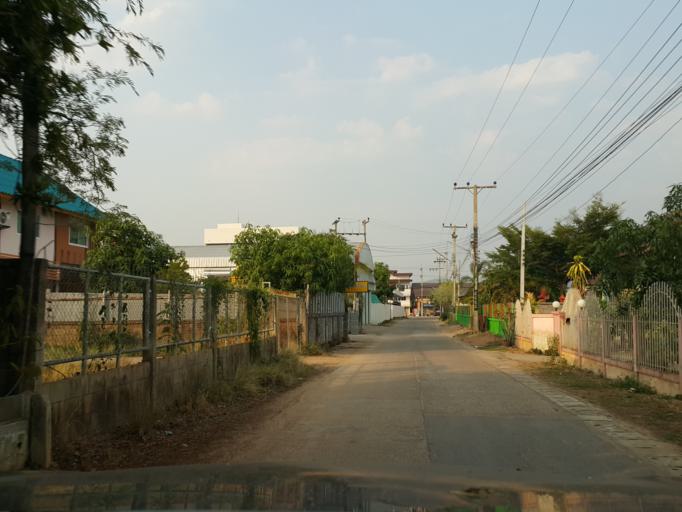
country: TH
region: Lamphun
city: Li
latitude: 17.8042
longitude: 98.9453
